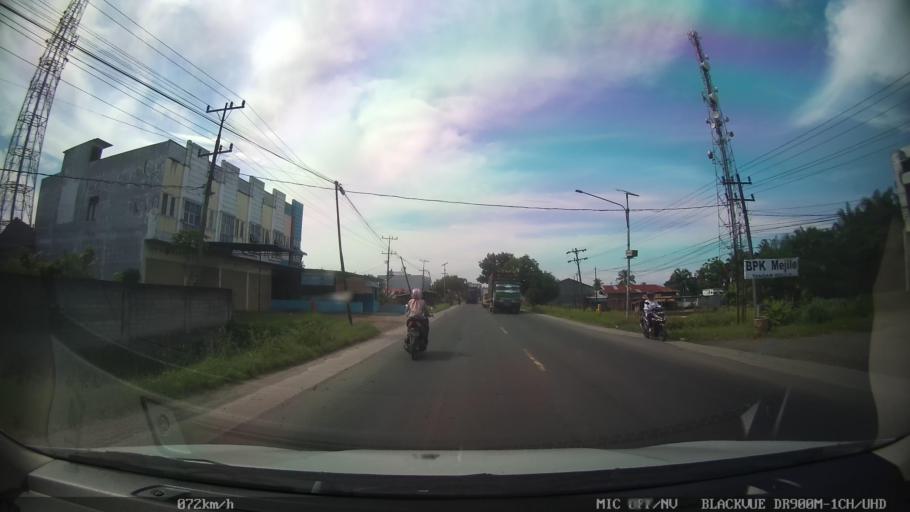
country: ID
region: North Sumatra
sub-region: Kabupaten Langkat
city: Stabat
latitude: 3.6838
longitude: 98.5089
